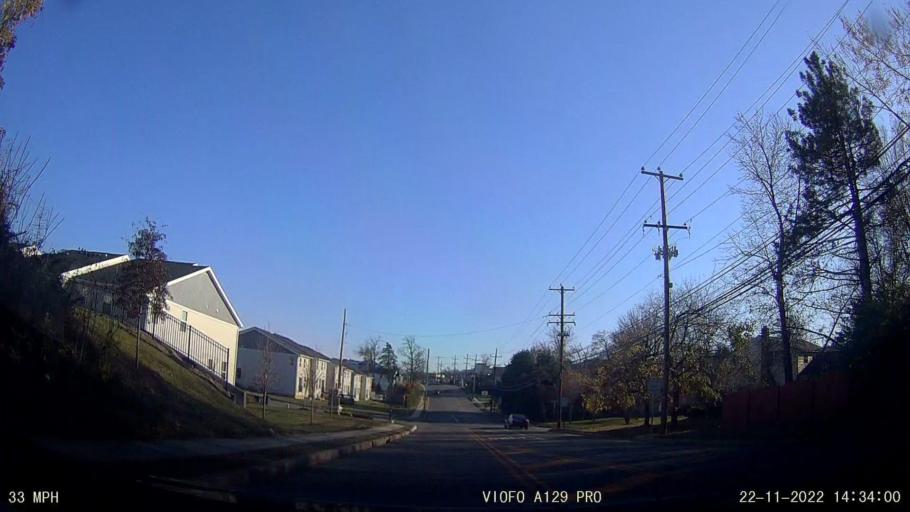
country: US
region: Pennsylvania
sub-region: Montgomery County
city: Bridgeport
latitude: 40.0985
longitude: -75.3670
